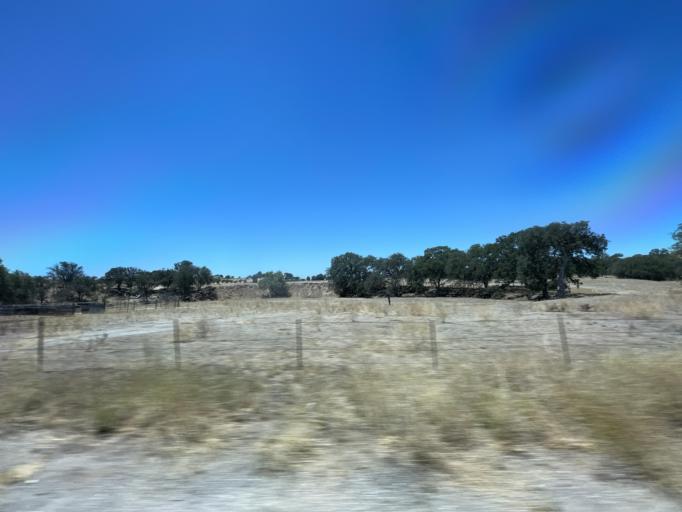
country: US
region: California
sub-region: San Luis Obispo County
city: Paso Robles
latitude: 35.6397
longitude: -120.5796
